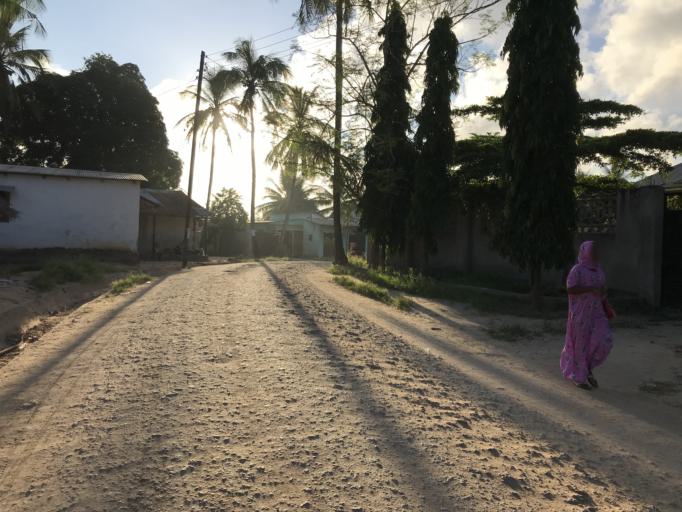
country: TZ
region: Dar es Salaam
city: Dar es Salaam
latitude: -6.8635
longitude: 39.3577
